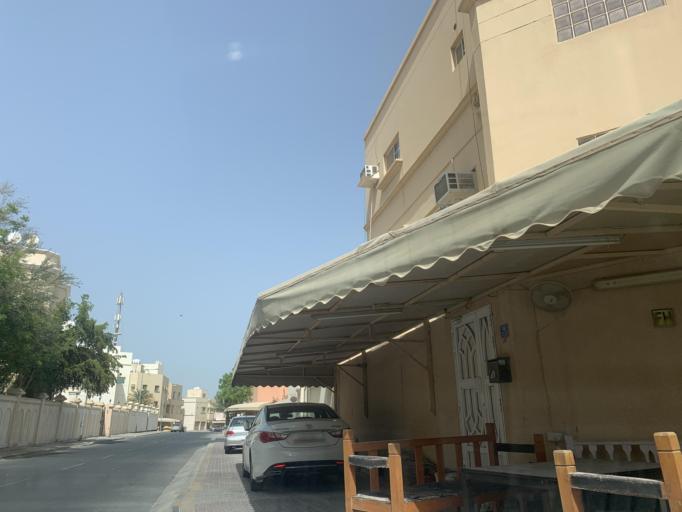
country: BH
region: Northern
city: Ar Rifa'
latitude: 26.1437
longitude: 50.5670
